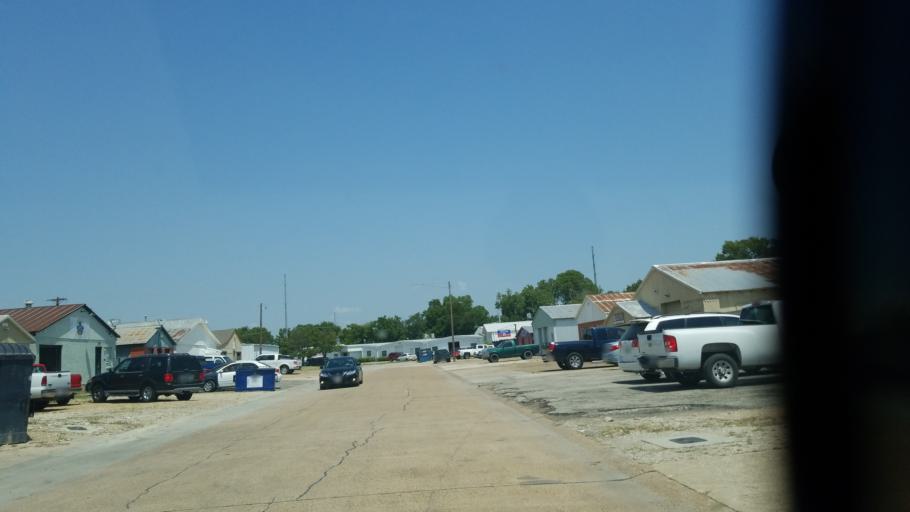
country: US
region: Texas
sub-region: Dallas County
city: Garland
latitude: 32.9123
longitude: -96.6266
